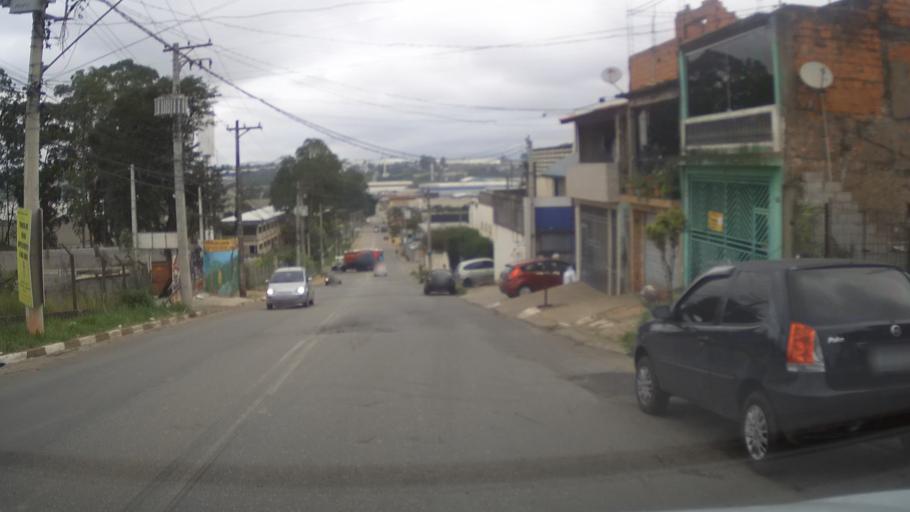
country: BR
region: Sao Paulo
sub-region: Aruja
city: Aruja
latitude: -23.4081
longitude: -46.3875
